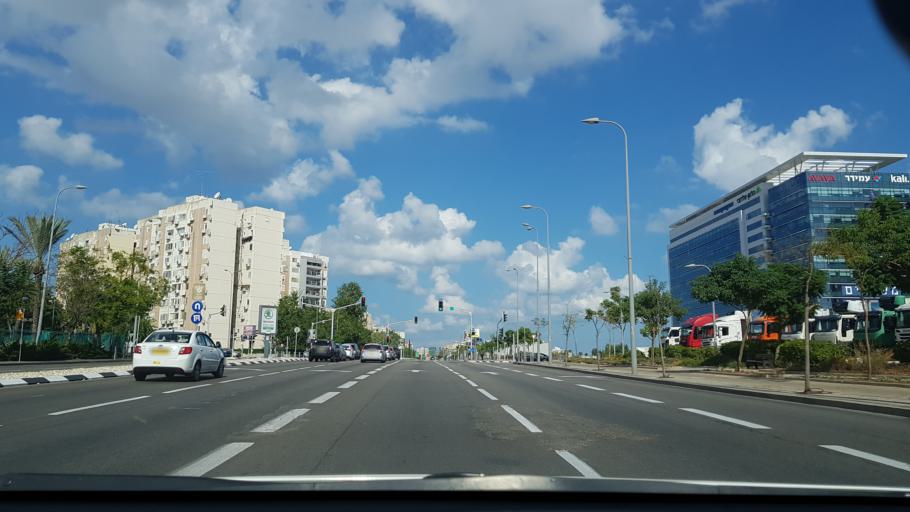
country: IL
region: Tel Aviv
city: Azor
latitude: 32.0051
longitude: 34.8000
